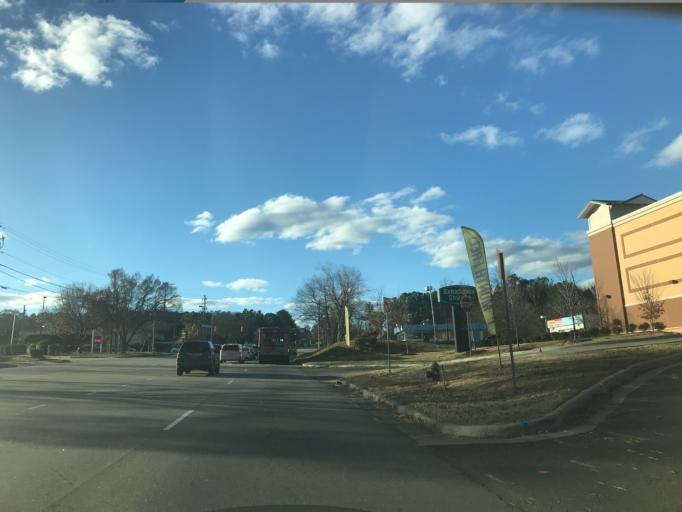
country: US
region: North Carolina
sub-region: Wake County
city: Raleigh
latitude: 35.8488
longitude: -78.6002
